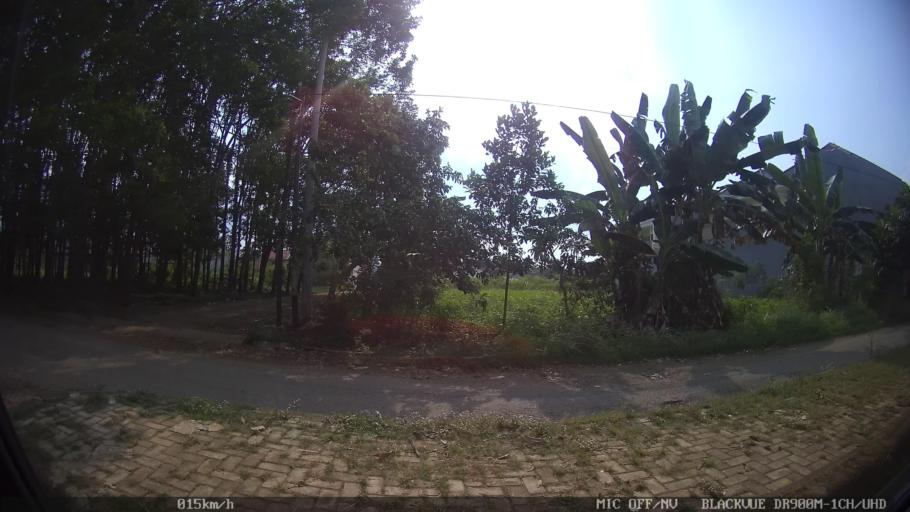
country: ID
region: Lampung
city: Kedaton
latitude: -5.3620
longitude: 105.2139
